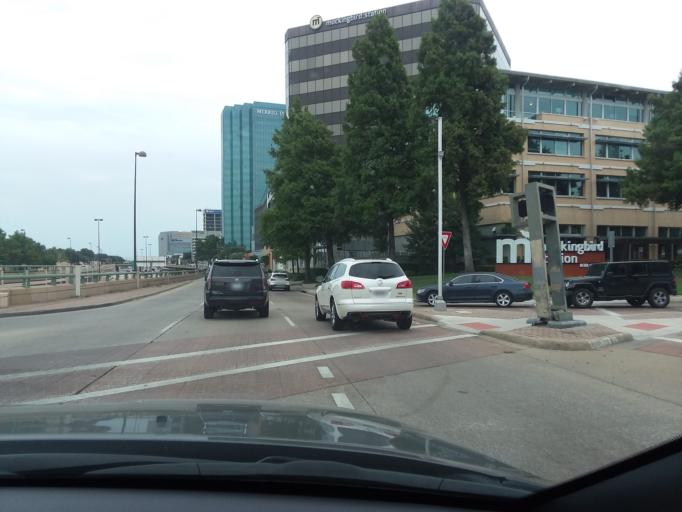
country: US
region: Texas
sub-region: Dallas County
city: Highland Park
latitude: 32.8367
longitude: -96.7782
